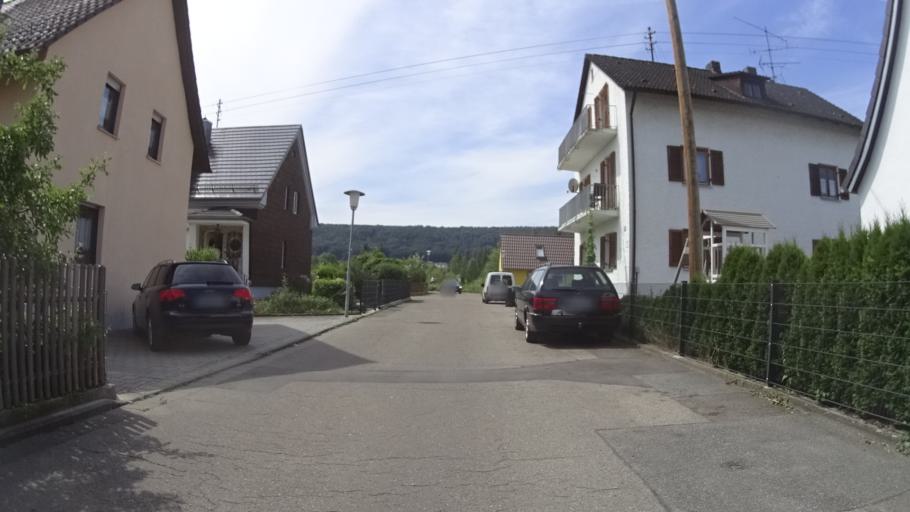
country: DE
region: Bavaria
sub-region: Lower Bavaria
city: Kelheim
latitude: 48.9158
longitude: 11.8819
